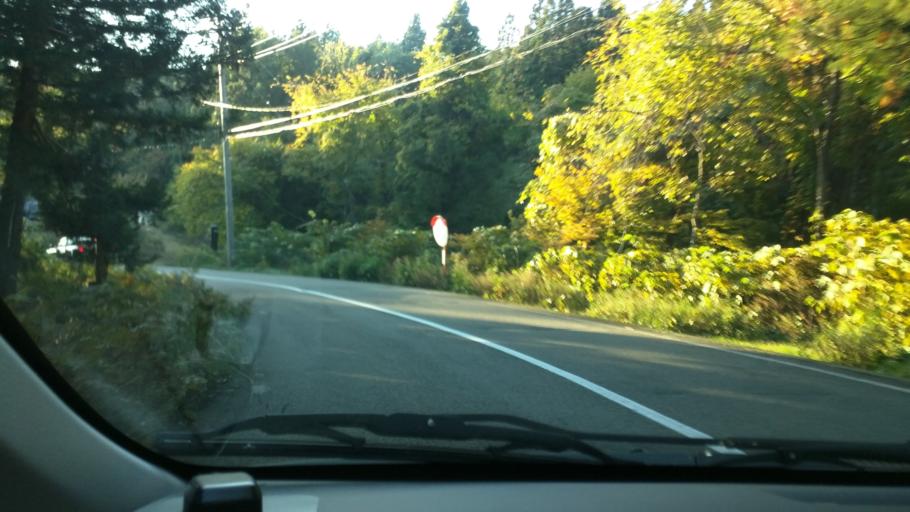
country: JP
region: Fukushima
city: Inawashiro
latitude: 37.5778
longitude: 140.0214
